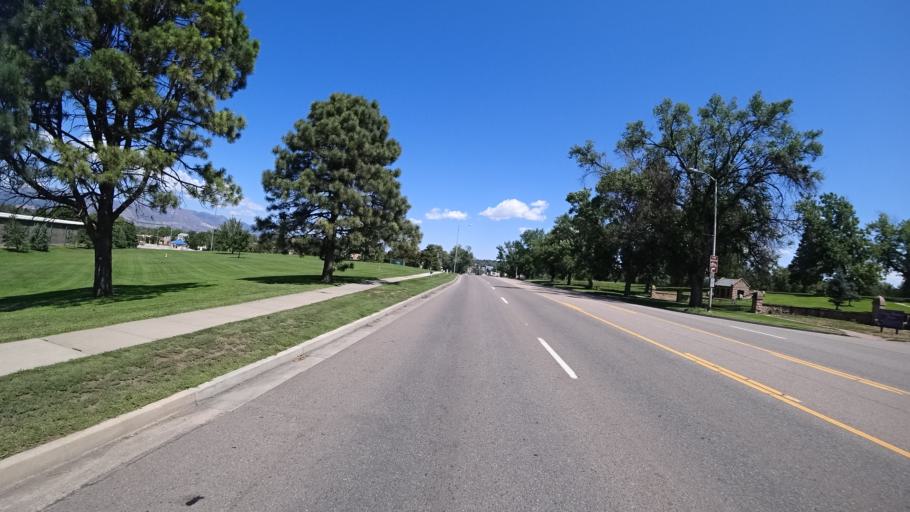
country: US
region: Colorado
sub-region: El Paso County
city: Colorado Springs
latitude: 38.8313
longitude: -104.7949
